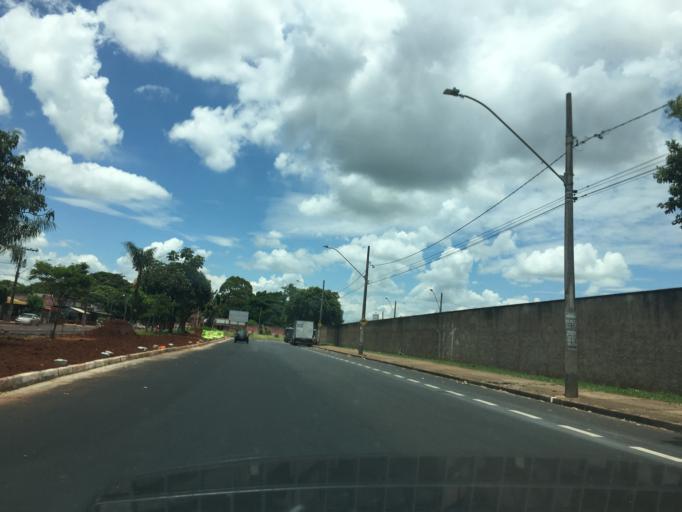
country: BR
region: Minas Gerais
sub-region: Uberlandia
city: Uberlandia
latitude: -18.9477
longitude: -48.3131
